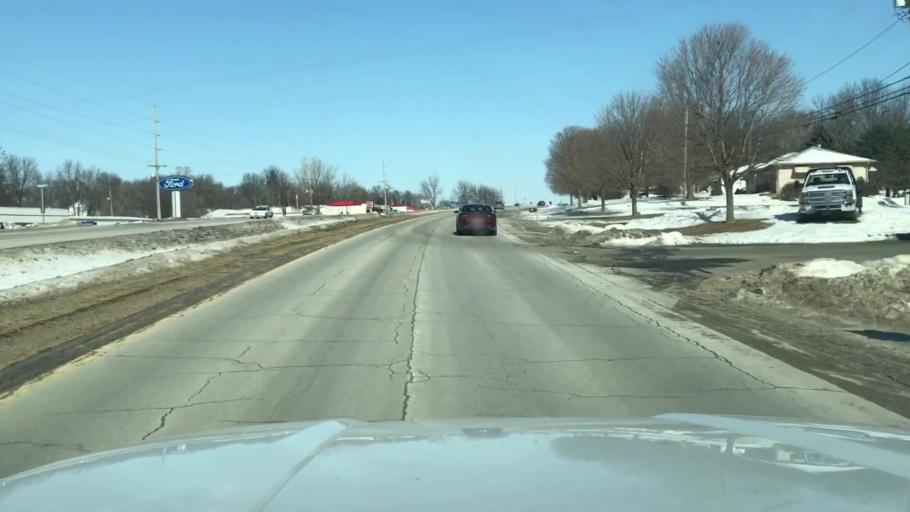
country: US
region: Missouri
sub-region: Andrew County
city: Savannah
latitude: 39.9348
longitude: -94.8215
